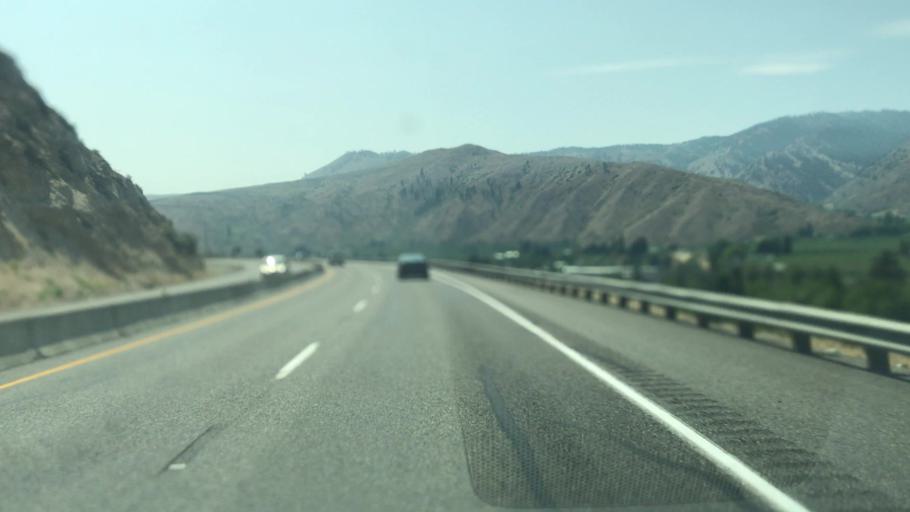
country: US
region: Washington
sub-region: Chelan County
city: Cashmere
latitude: 47.4939
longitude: -120.4207
